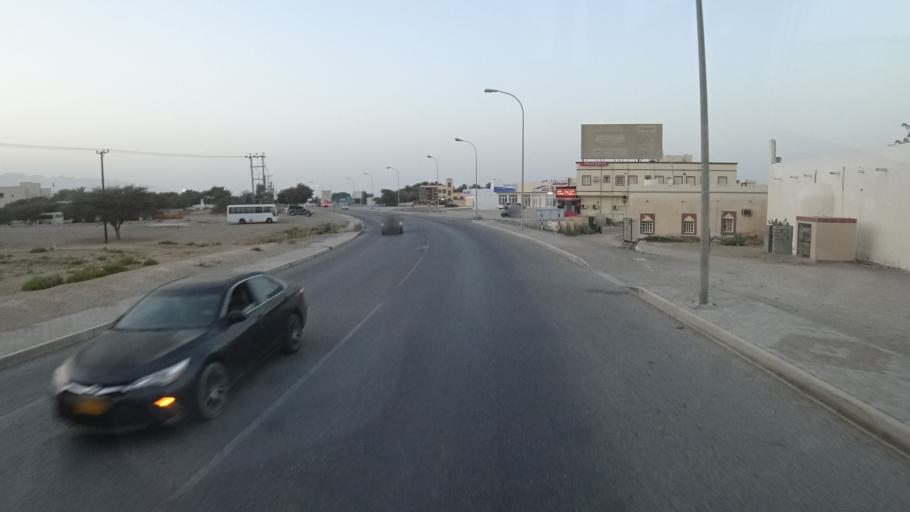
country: OM
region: Ash Sharqiyah
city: Sur
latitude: 22.5443
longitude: 59.4832
